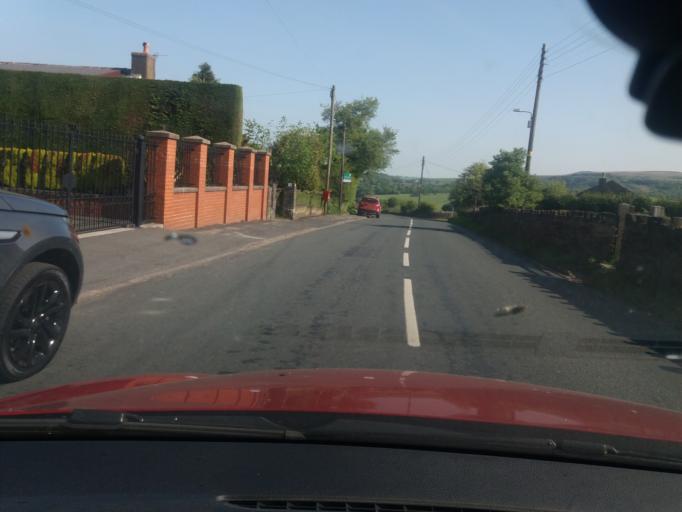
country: GB
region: England
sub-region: Lancashire
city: Adlington
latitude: 53.6265
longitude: -2.5882
